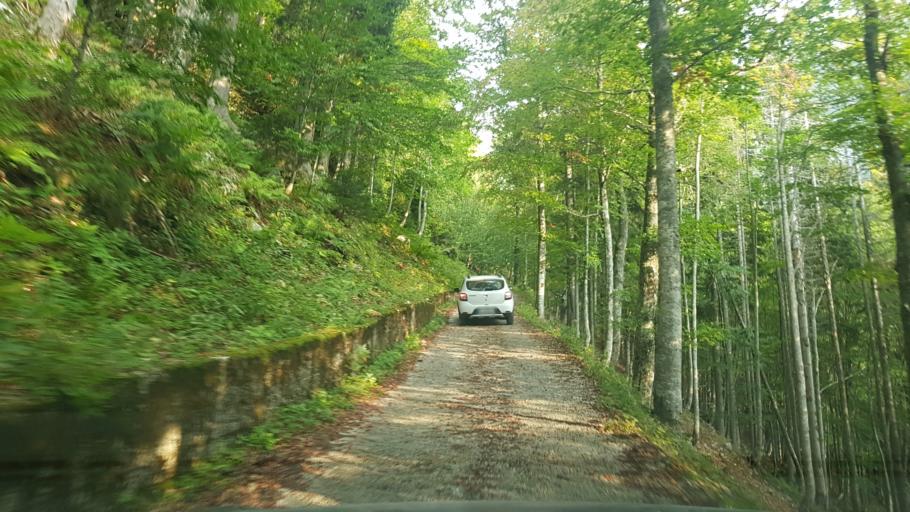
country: SI
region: Bovec
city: Bovec
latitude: 46.4096
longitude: 13.5094
